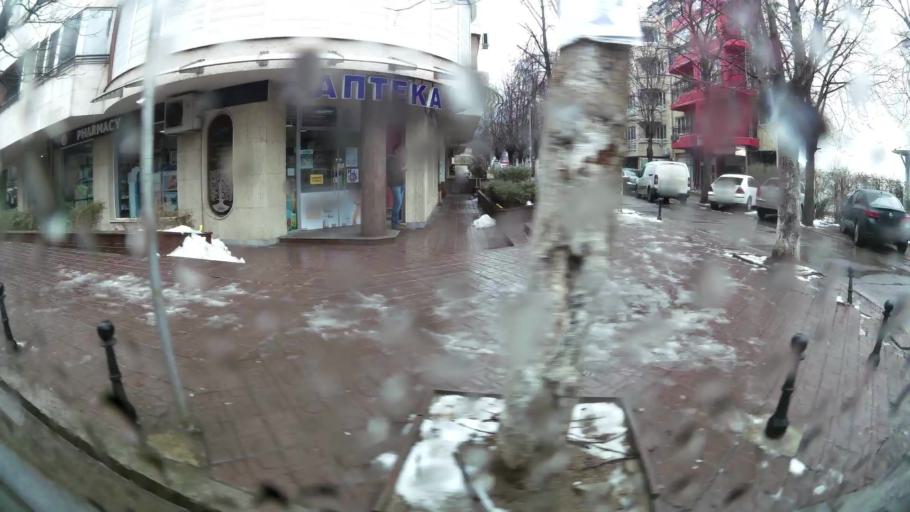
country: BG
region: Sofia-Capital
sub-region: Stolichna Obshtina
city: Sofia
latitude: 42.6722
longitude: 23.2967
